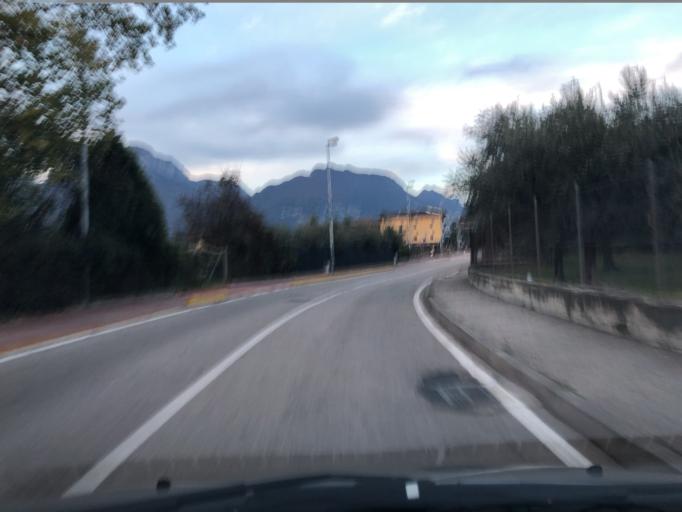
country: IT
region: Trentino-Alto Adige
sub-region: Provincia di Trento
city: Torbole sul Garda
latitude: 45.8836
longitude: 10.8626
